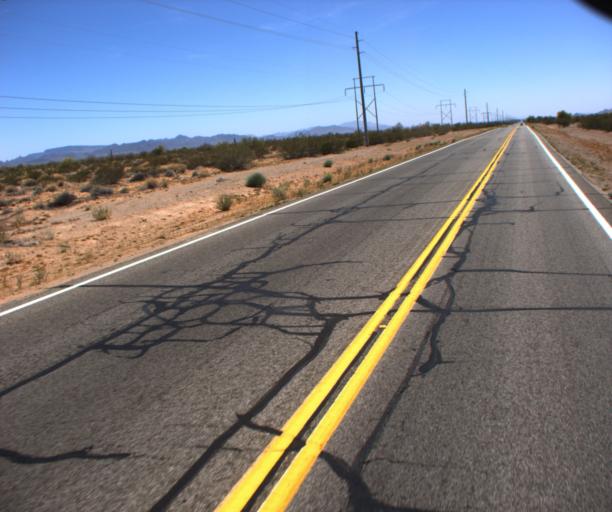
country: US
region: Arizona
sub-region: La Paz County
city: Quartzsite
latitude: 33.7894
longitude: -114.2170
